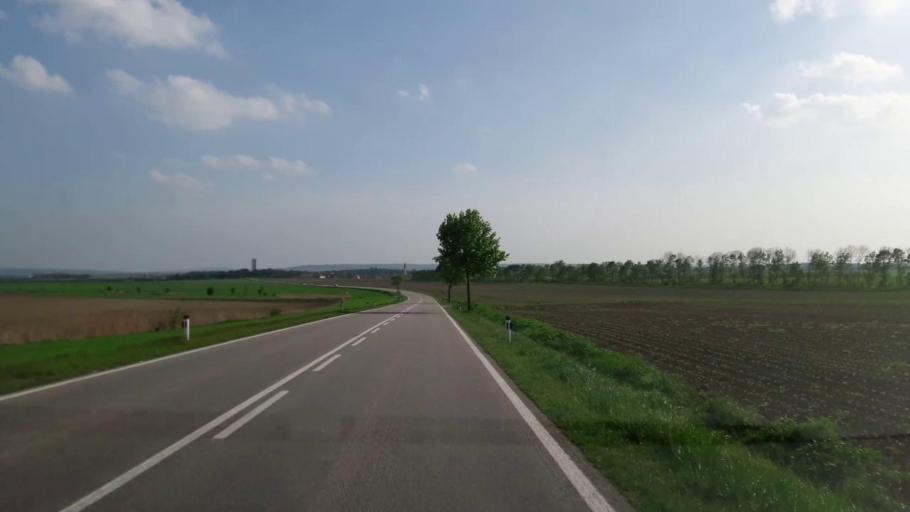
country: AT
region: Lower Austria
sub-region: Politischer Bezirk Hollabrunn
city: Guntersdorf
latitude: 48.6649
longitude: 16.0521
